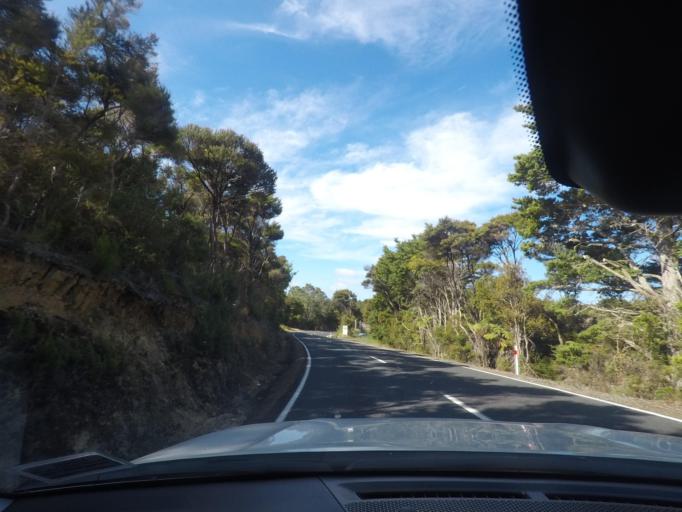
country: NZ
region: Northland
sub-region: Whangarei
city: Ngunguru
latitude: -35.6658
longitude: 174.4778
